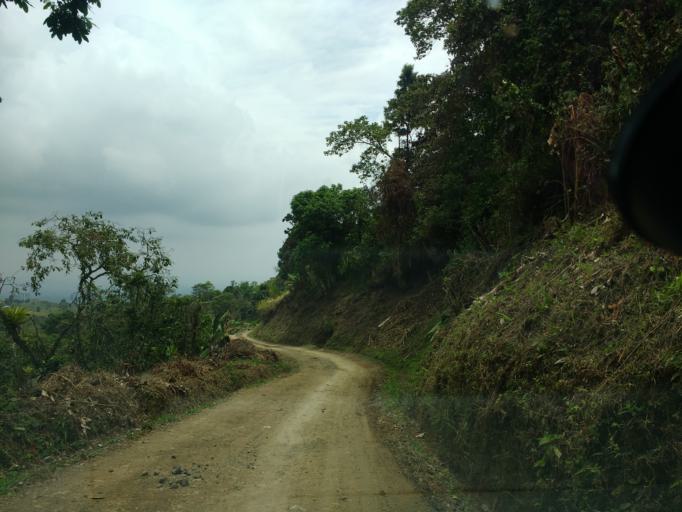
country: CO
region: Cauca
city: Santander de Quilichao
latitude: 2.9195
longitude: -76.4667
